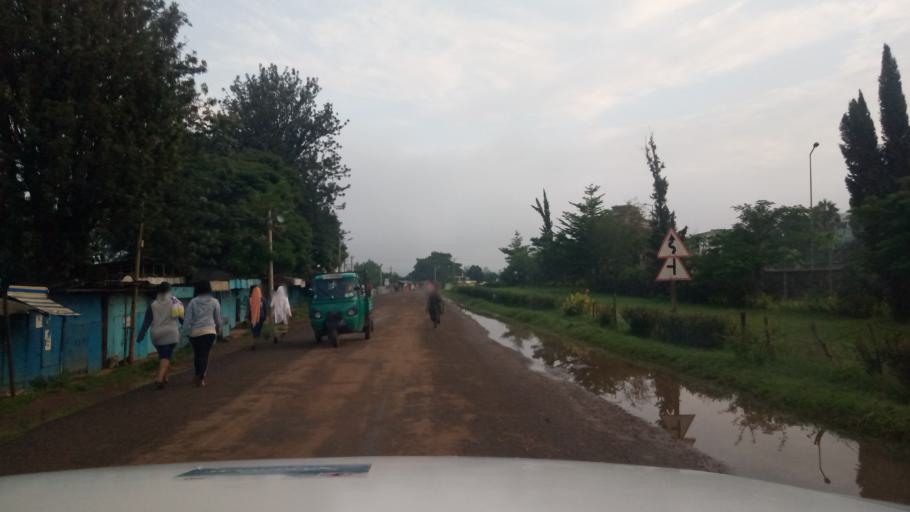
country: ET
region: Oromiya
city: Jima
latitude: 7.6774
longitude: 36.8515
